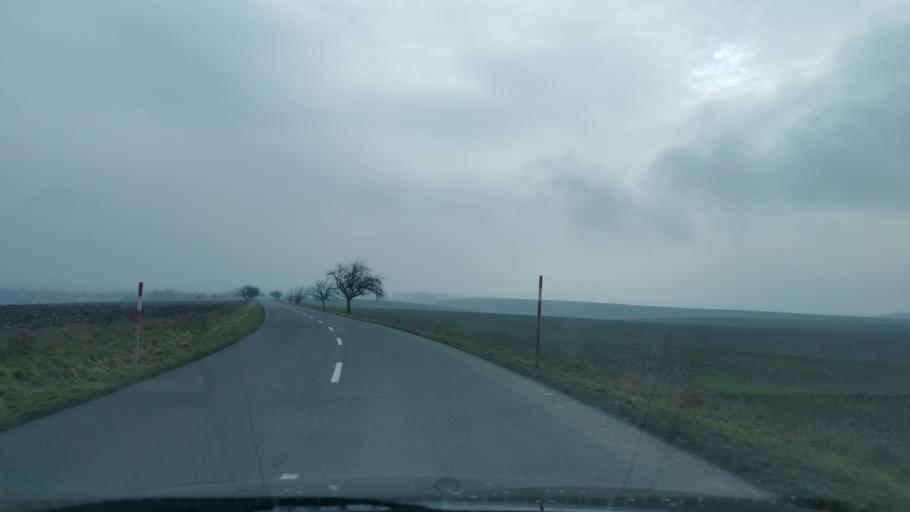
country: SK
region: Trnavsky
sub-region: Okres Senica
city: Senica
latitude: 48.7164
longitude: 17.3238
